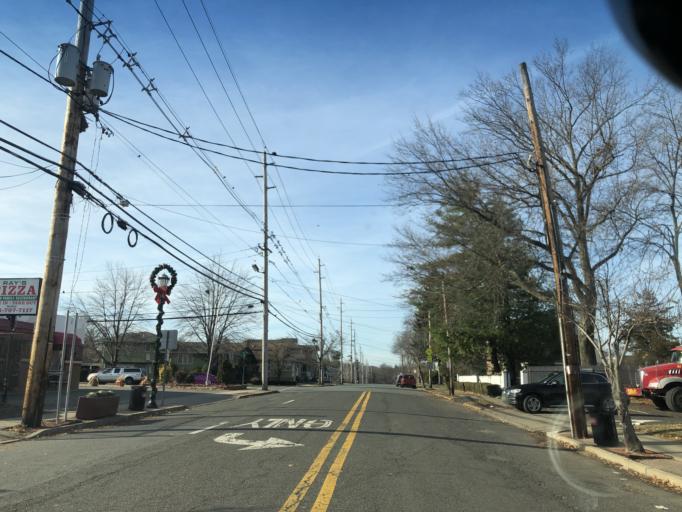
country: US
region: New Jersey
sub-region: Bergen County
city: Fair Lawn
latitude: 40.9310
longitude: -74.1321
